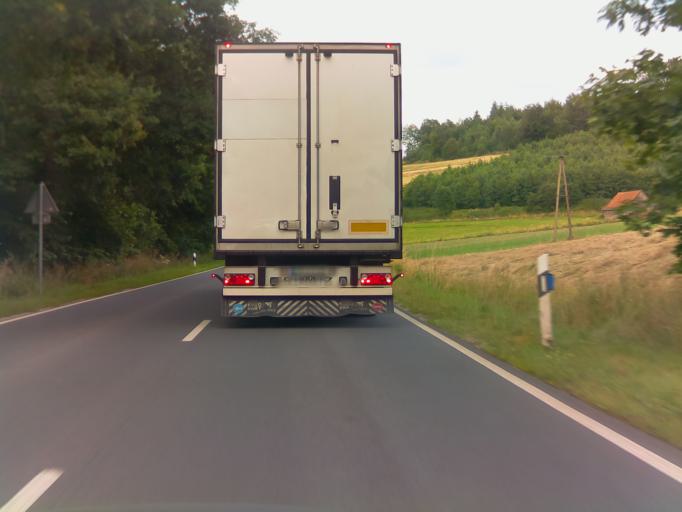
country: DE
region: Hesse
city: Grebenau
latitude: 50.7781
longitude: 9.4620
